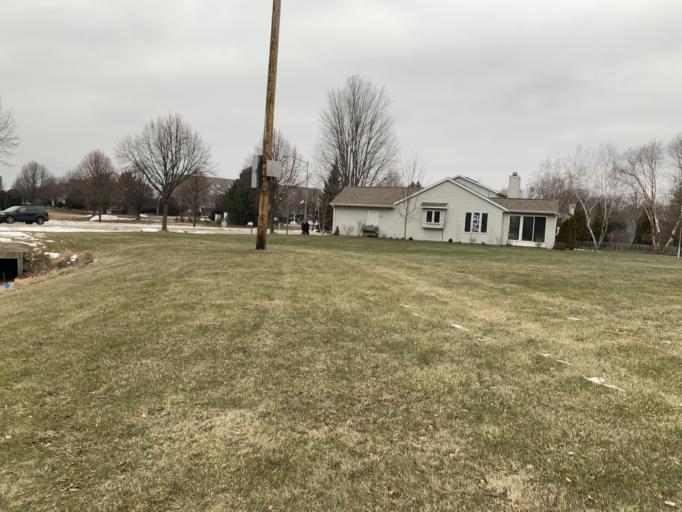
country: US
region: Wisconsin
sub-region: Dane County
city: Middleton
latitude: 43.0804
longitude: -89.5188
